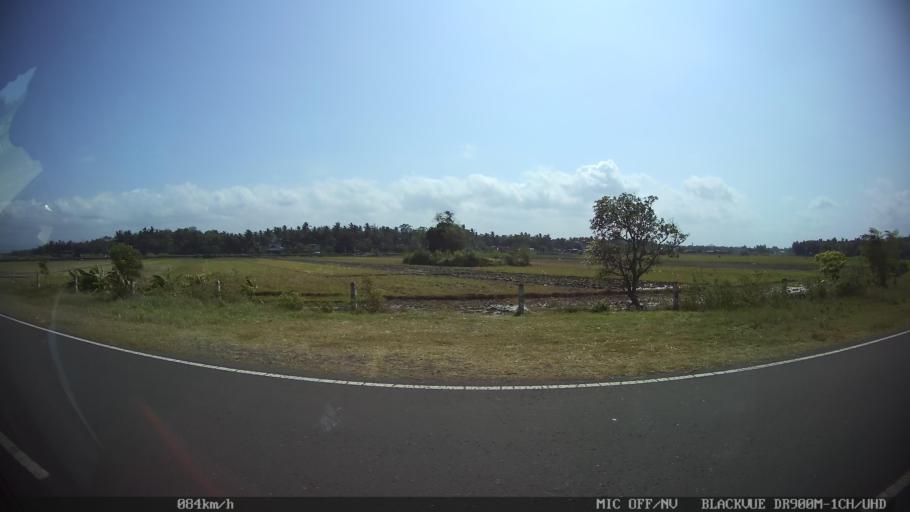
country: ID
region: Daerah Istimewa Yogyakarta
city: Srandakan
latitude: -7.9550
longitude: 110.1970
